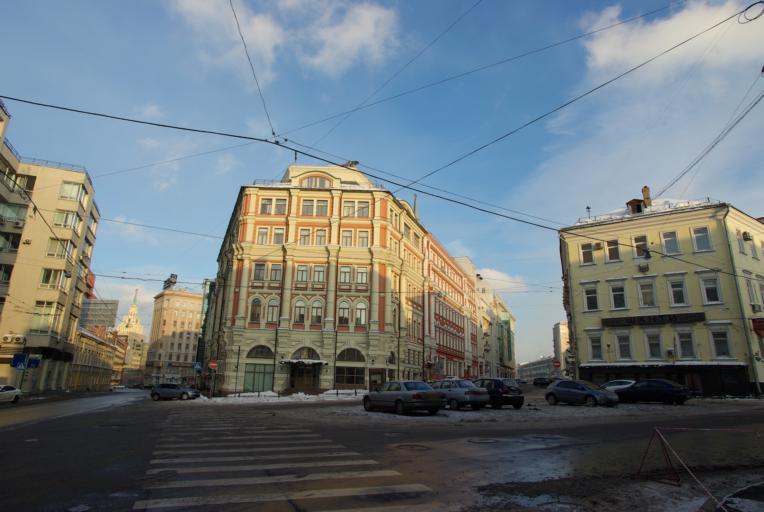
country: RU
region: Moscow
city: Moscow
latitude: 55.7683
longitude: 37.6447
